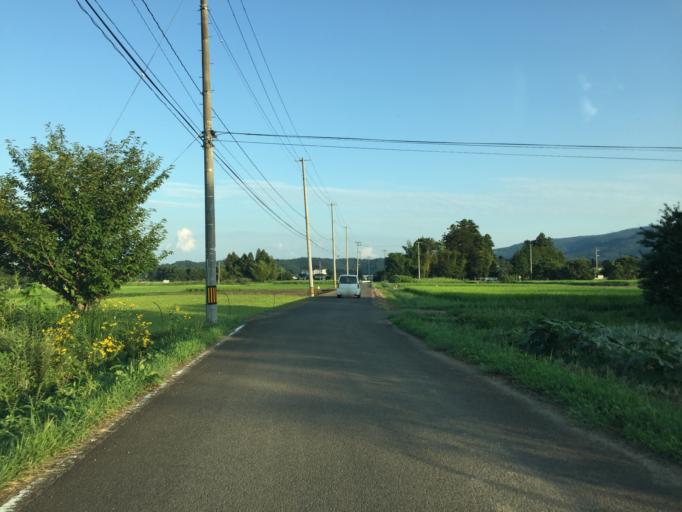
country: JP
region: Fukushima
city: Fukushima-shi
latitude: 37.7261
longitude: 140.3783
